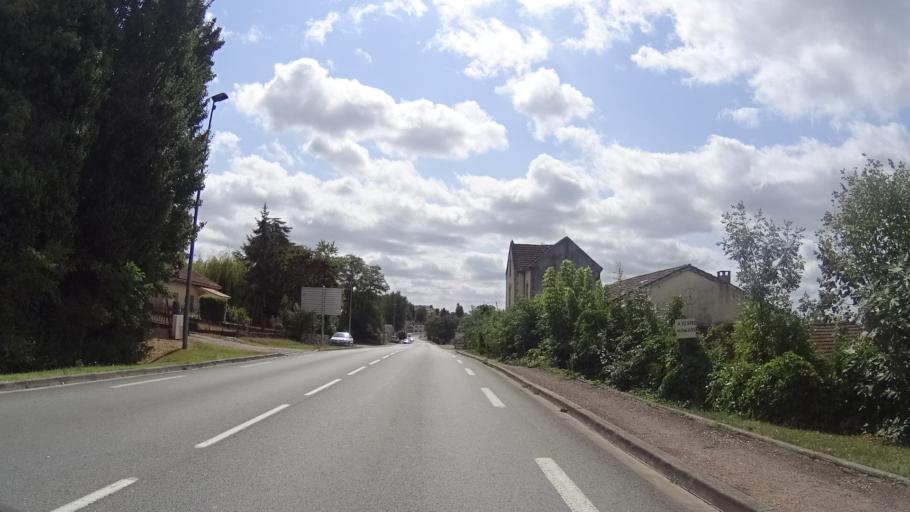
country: FR
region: Aquitaine
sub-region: Departement du Lot-et-Garonne
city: Foulayronnes
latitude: 44.2438
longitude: 0.6440
